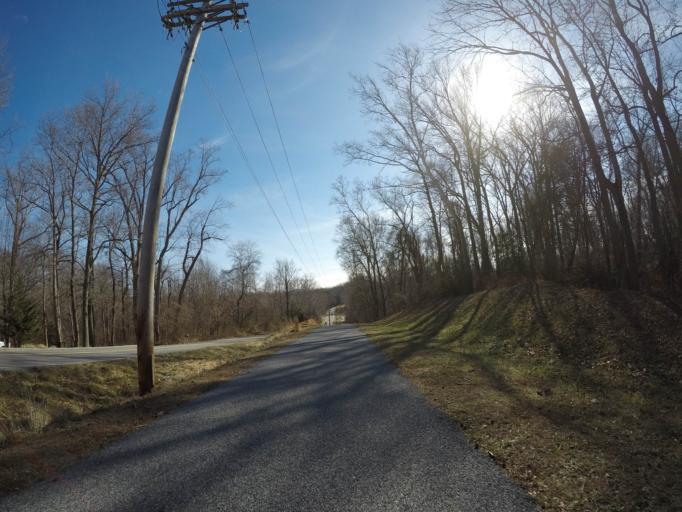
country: US
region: Maryland
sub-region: Charles County
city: Bennsville
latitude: 38.5978
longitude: -77.0166
